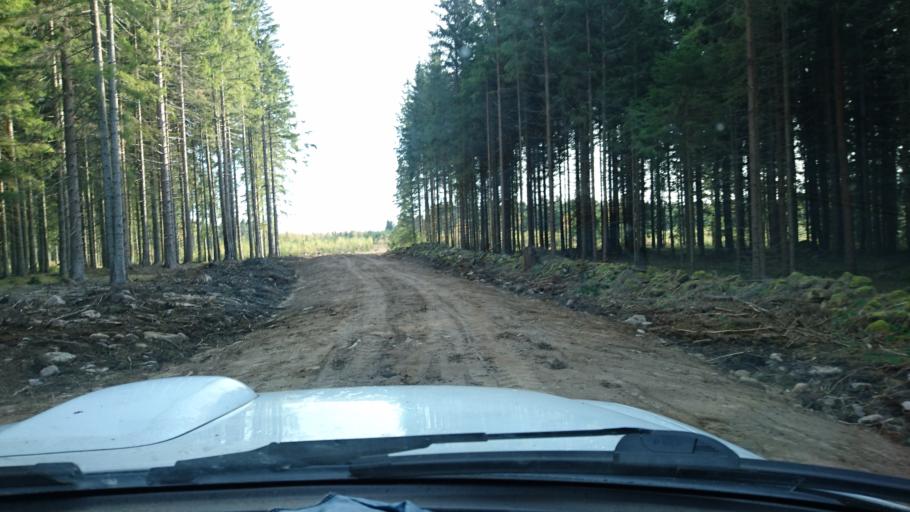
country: SE
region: Vaestra Goetaland
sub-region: Ulricehamns Kommun
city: Ulricehamn
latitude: 57.9369
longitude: 13.5568
